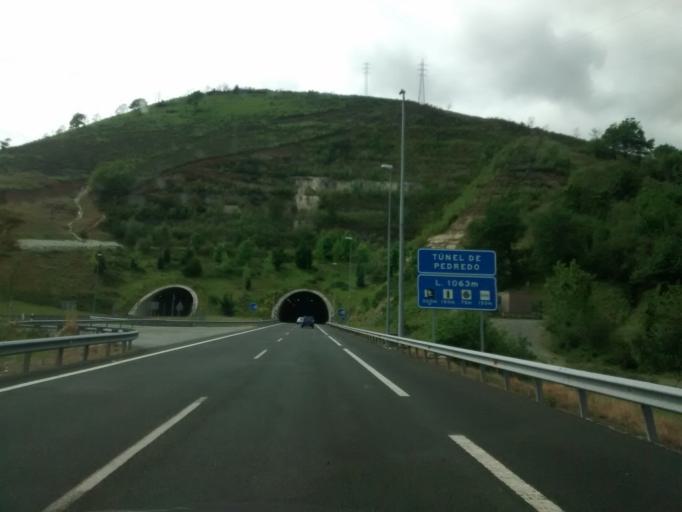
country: ES
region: Cantabria
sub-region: Provincia de Cantabria
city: Arenas de Iguna
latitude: 43.2144
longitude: -4.0781
